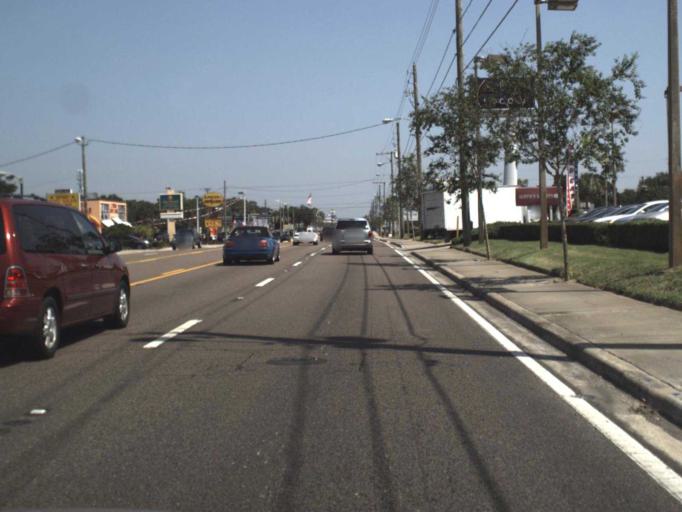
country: US
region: Florida
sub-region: Hillsborough County
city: Lake Magdalene
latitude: 28.0453
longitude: -82.4593
